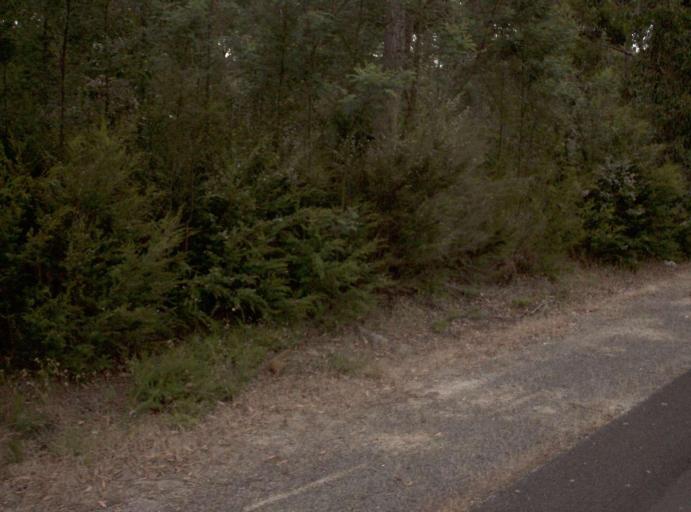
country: AU
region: Victoria
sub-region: Wellington
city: Sale
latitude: -38.4632
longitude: 146.9335
